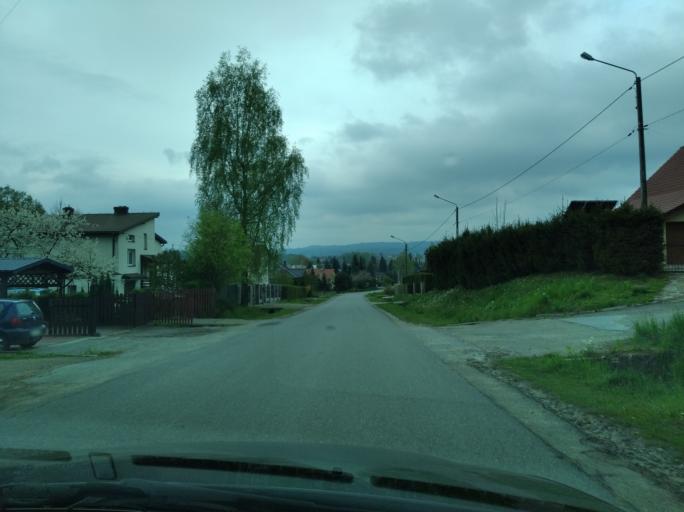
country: PL
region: Subcarpathian Voivodeship
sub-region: Powiat sanocki
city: Sanok
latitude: 49.5557
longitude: 22.2309
